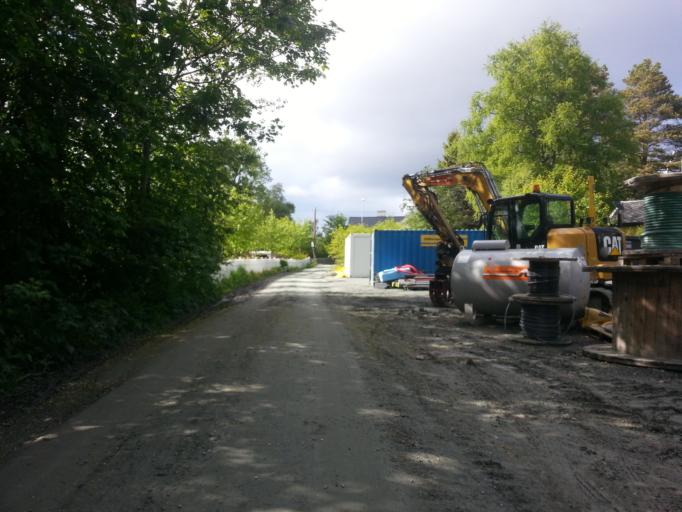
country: NO
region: Sor-Trondelag
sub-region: Trondheim
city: Trondheim
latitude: 63.4171
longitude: 10.4103
